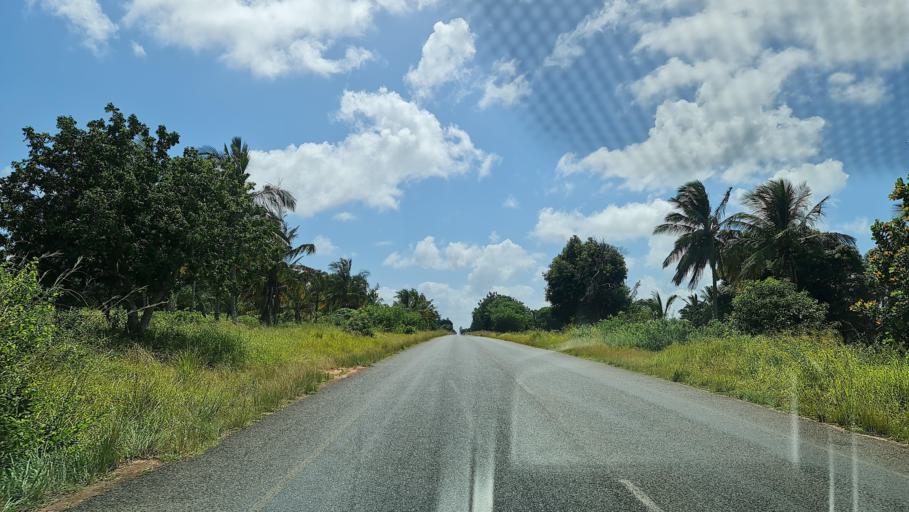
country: MZ
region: Inhambane
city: Maxixe
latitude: -24.5348
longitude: 34.9426
